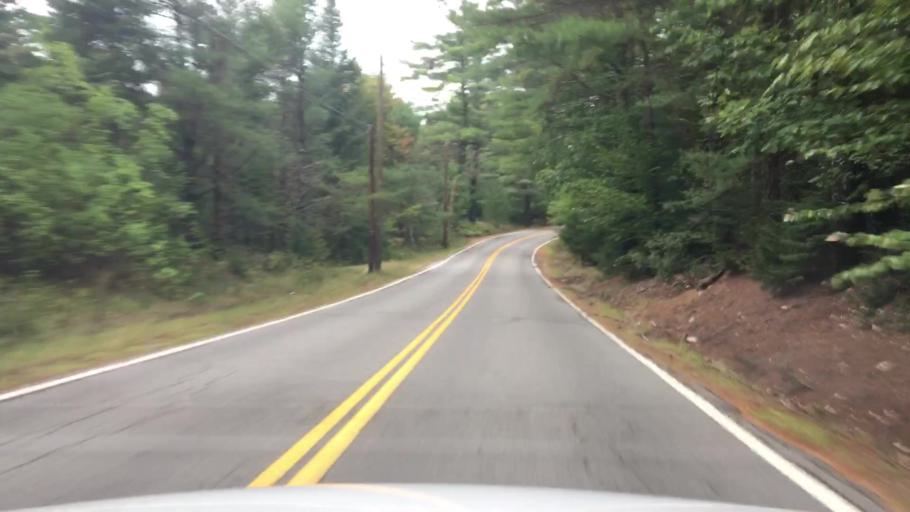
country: US
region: New Hampshire
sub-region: Carroll County
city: Effingham
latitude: 43.7200
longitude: -70.9974
